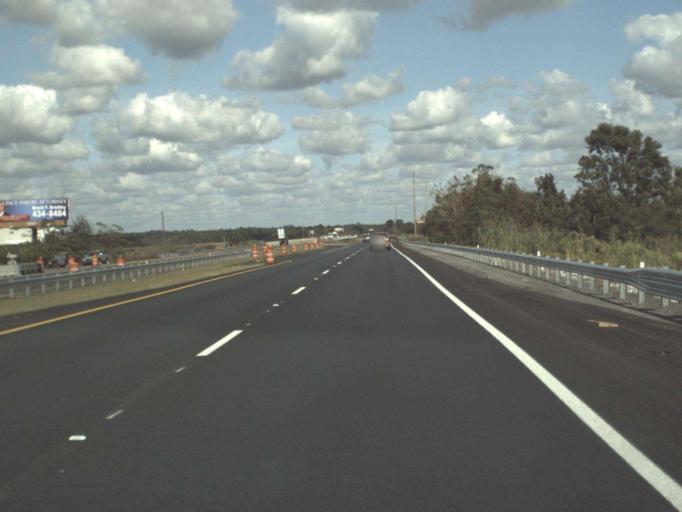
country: US
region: Florida
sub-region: Santa Rosa County
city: Pace
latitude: 30.5731
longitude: -87.1838
